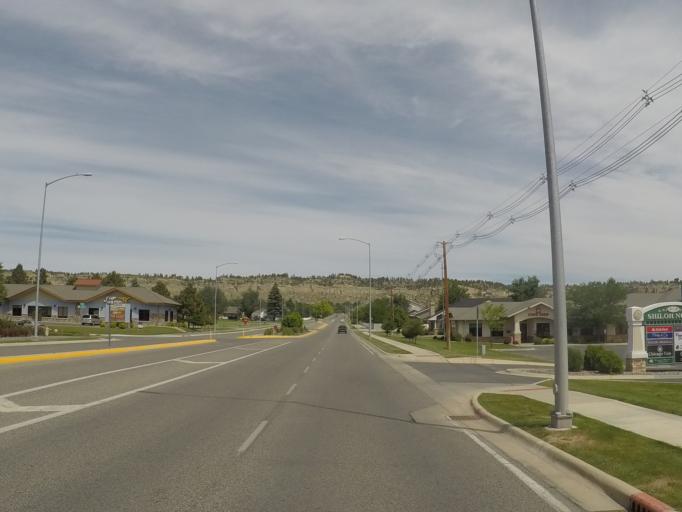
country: US
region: Montana
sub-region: Yellowstone County
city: Billings
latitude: 45.7866
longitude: -108.6175
